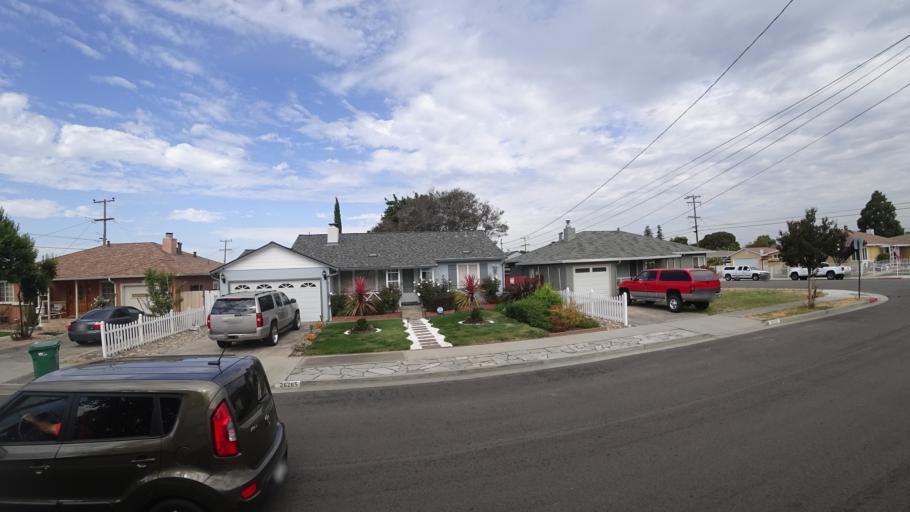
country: US
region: California
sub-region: Alameda County
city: Hayward
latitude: 37.6472
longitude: -122.0707
